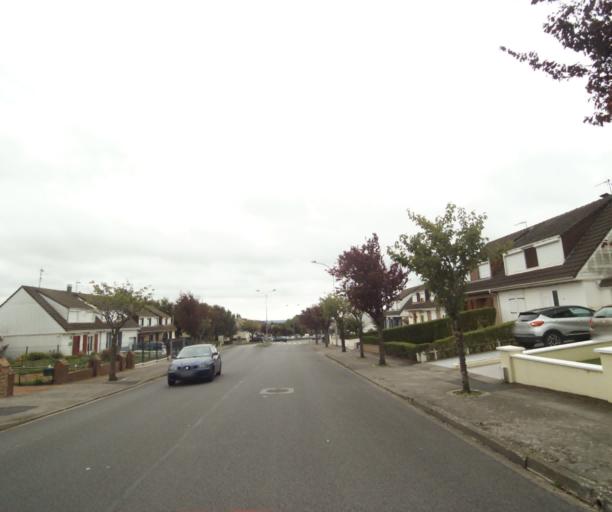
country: FR
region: Nord-Pas-de-Calais
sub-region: Departement du Pas-de-Calais
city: Etaples
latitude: 50.5234
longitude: 1.6390
